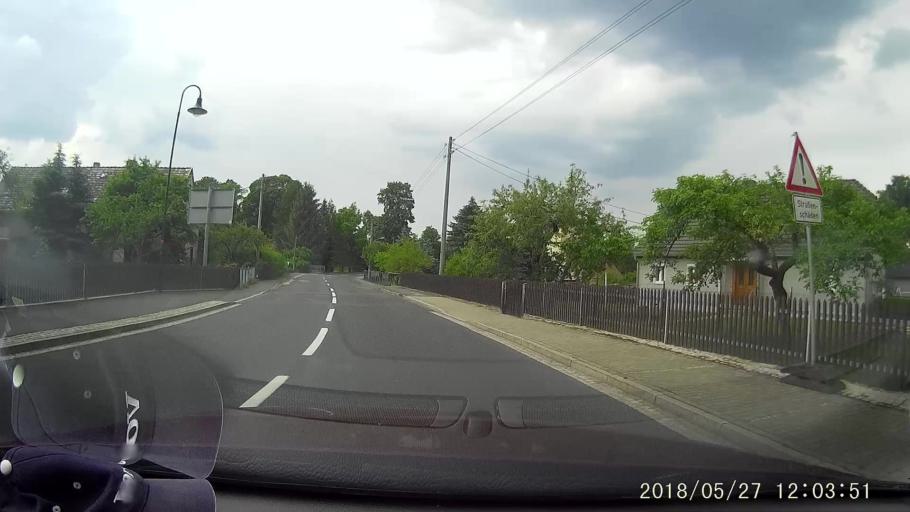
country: DE
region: Saxony
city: Mucka
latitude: 51.3464
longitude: 14.6846
